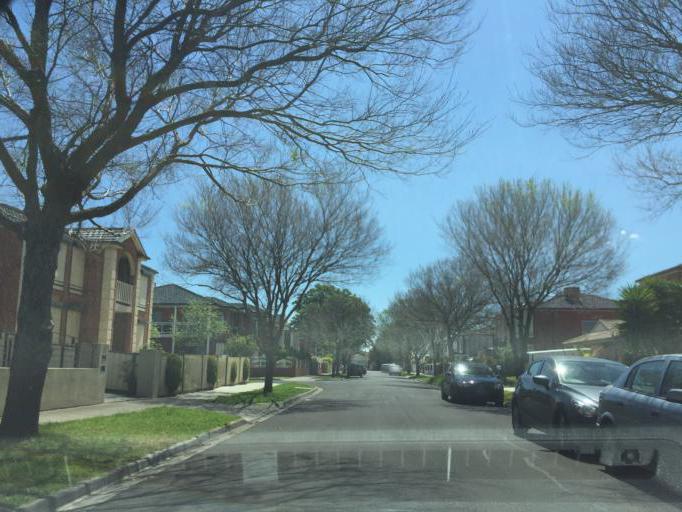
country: AU
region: Victoria
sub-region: Maribyrnong
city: Braybrook
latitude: -37.7915
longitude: 144.8556
